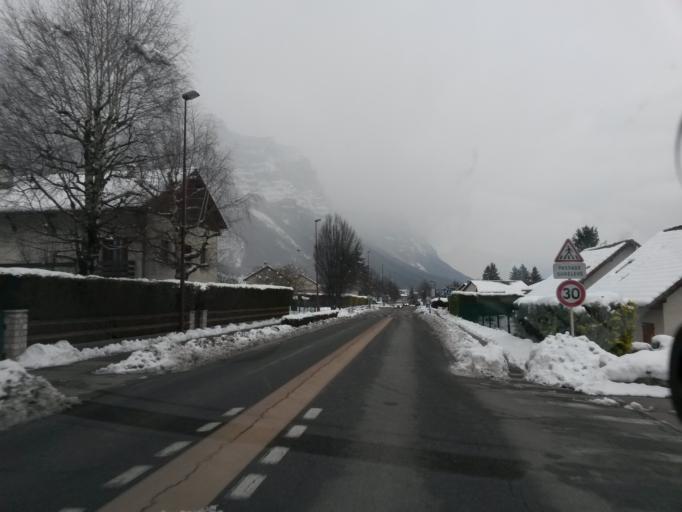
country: FR
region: Rhone-Alpes
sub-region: Departement de l'Isere
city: Bernin
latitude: 45.2746
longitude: 5.8707
